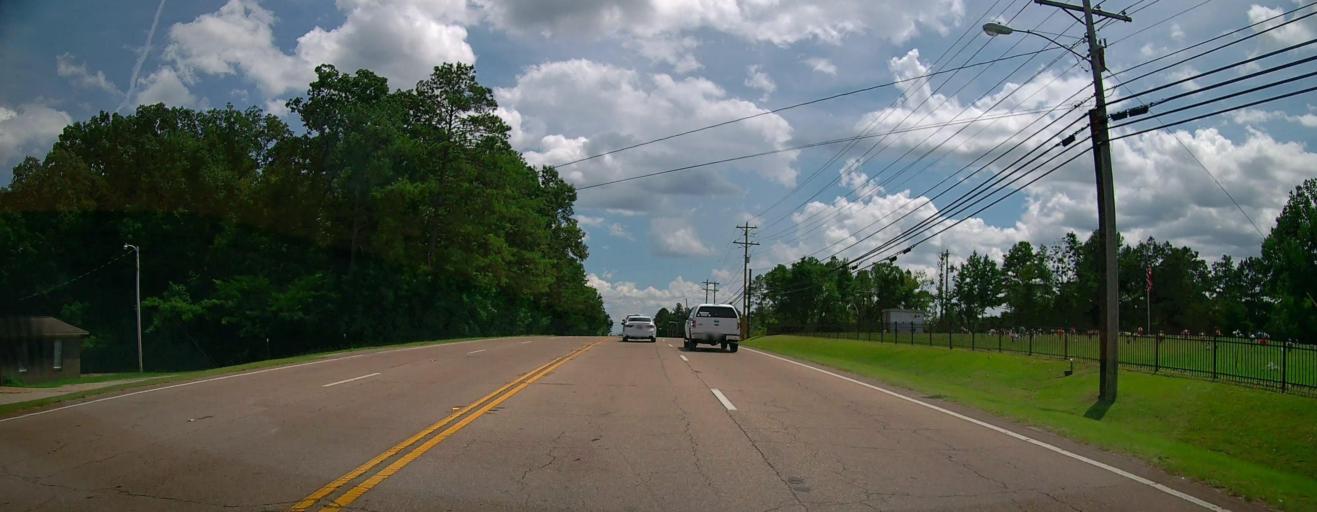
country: US
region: Mississippi
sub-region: Lee County
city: Verona
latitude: 34.1756
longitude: -88.7198
